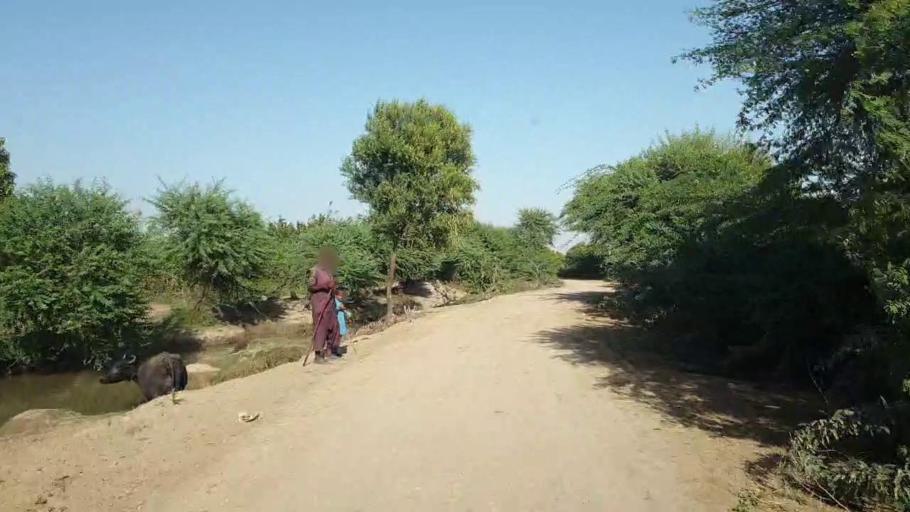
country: PK
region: Sindh
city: Badin
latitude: 24.6048
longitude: 68.9231
